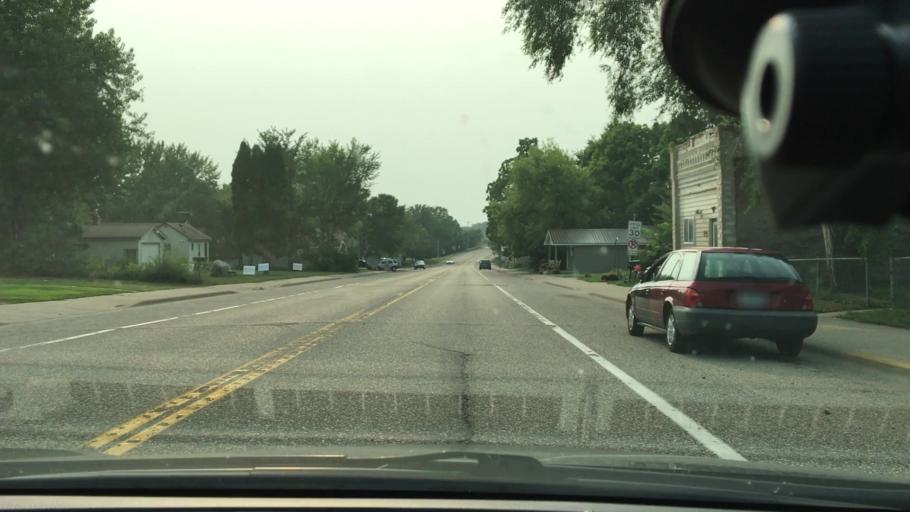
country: US
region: Minnesota
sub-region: Hennepin County
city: Dayton
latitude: 45.2442
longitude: -93.5171
